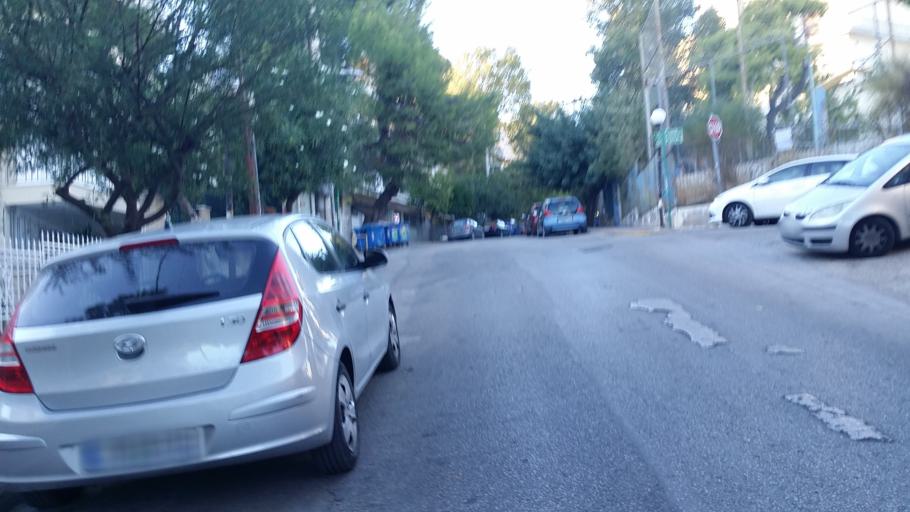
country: GR
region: Attica
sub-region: Nomarchia Athinas
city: Irakleio
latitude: 38.0483
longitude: 23.7596
